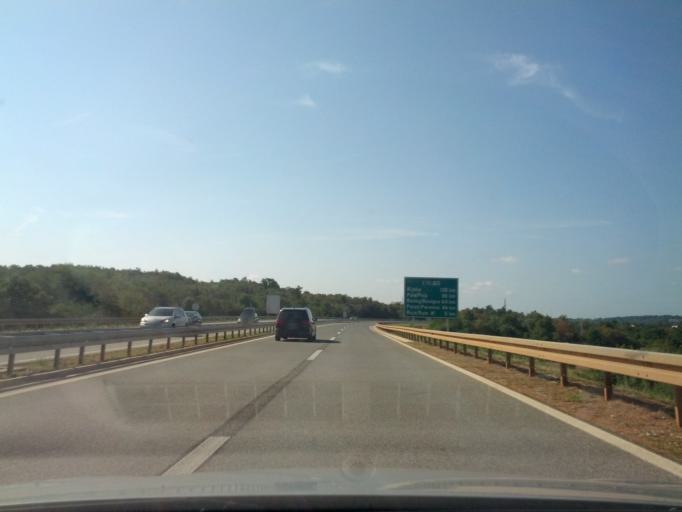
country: SI
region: Piran-Pirano
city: Seca
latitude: 45.4461
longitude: 13.6181
